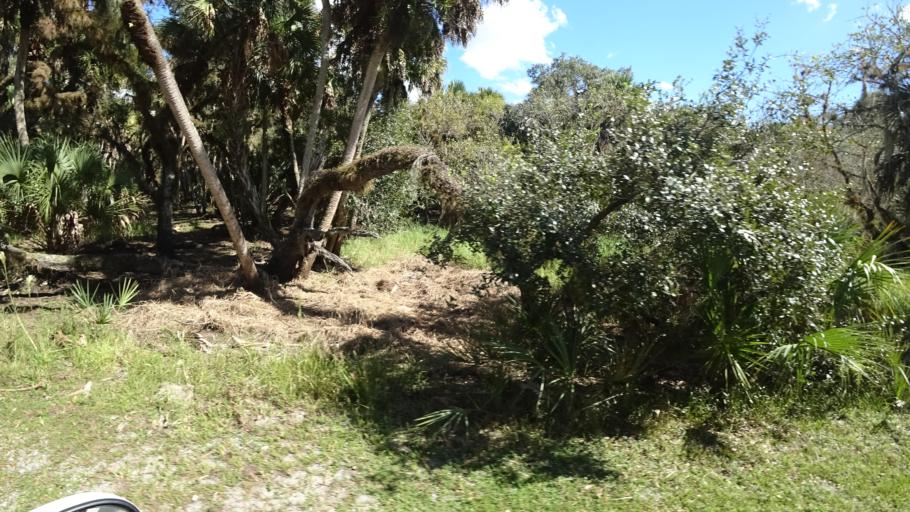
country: US
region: Florida
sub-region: Sarasota County
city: Lake Sarasota
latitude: 27.2485
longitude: -82.2950
